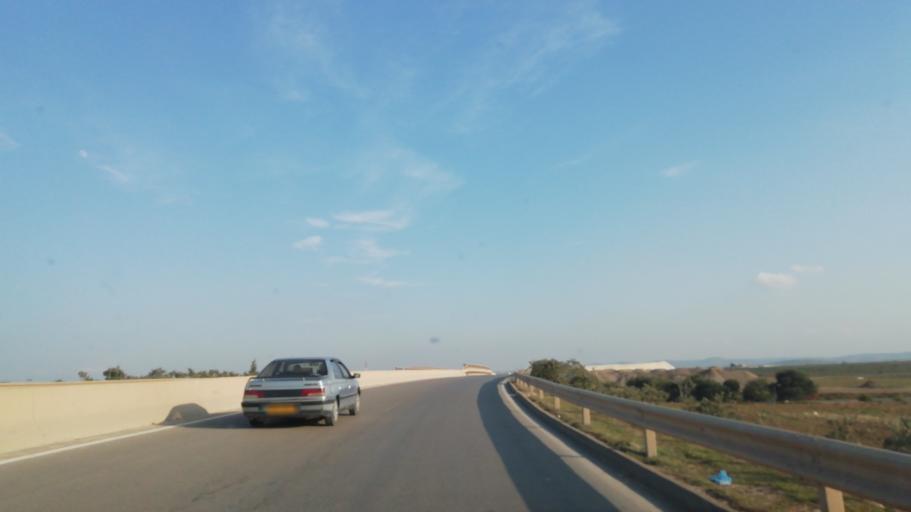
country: DZ
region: Relizane
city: Djidiouia
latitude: 35.8975
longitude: 0.7097
